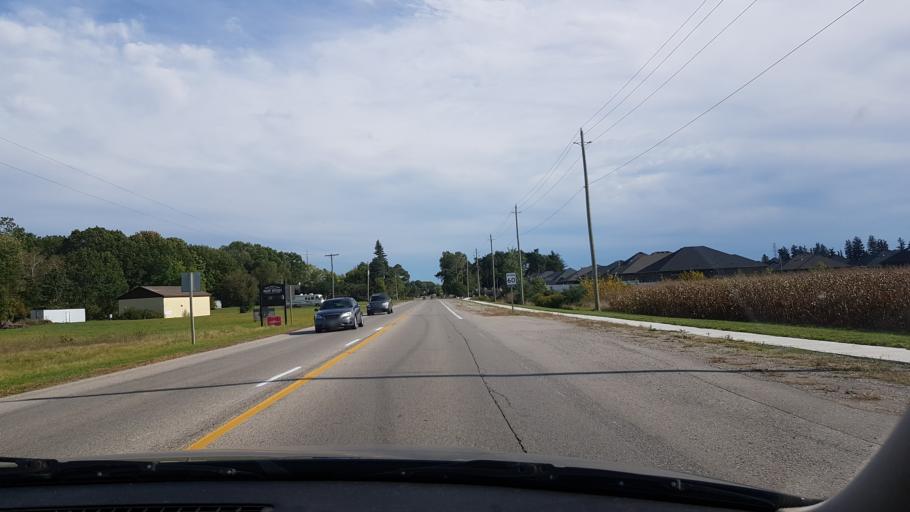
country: CA
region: Ontario
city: Delaware
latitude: 42.9018
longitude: -81.4802
